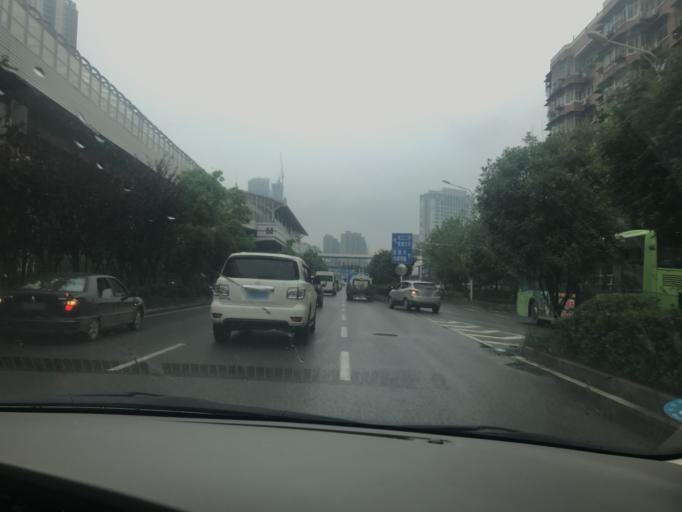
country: CN
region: Hubei
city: Jiang'an
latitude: 30.6219
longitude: 114.3093
